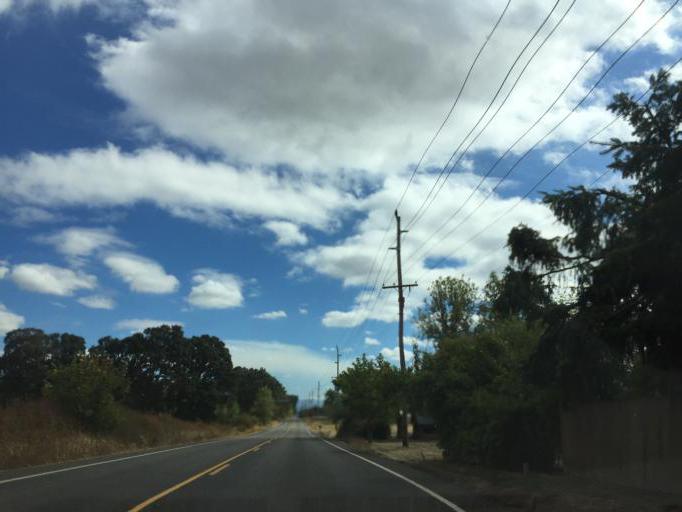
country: US
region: Oregon
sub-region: Marion County
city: Mount Angel
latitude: 45.1176
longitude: -122.7966
